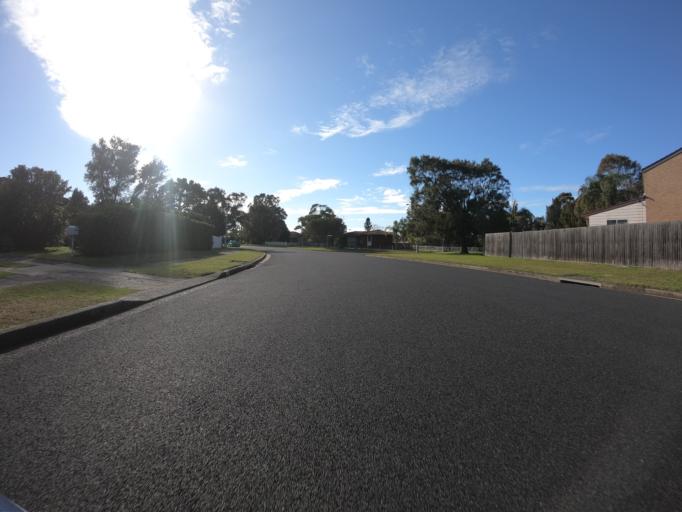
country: AU
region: New South Wales
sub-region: Wollongong
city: East Corrimal
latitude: -34.3712
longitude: 150.9187
